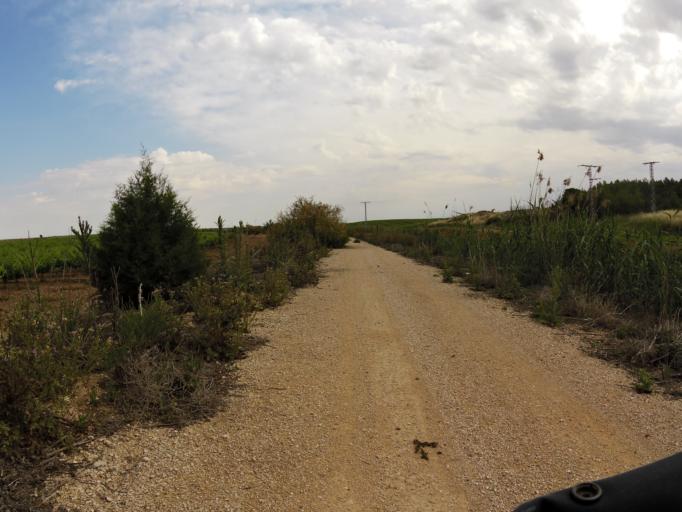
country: ES
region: Castille-La Mancha
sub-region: Provincia de Albacete
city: Valdeganga
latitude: 39.0522
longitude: -1.7566
